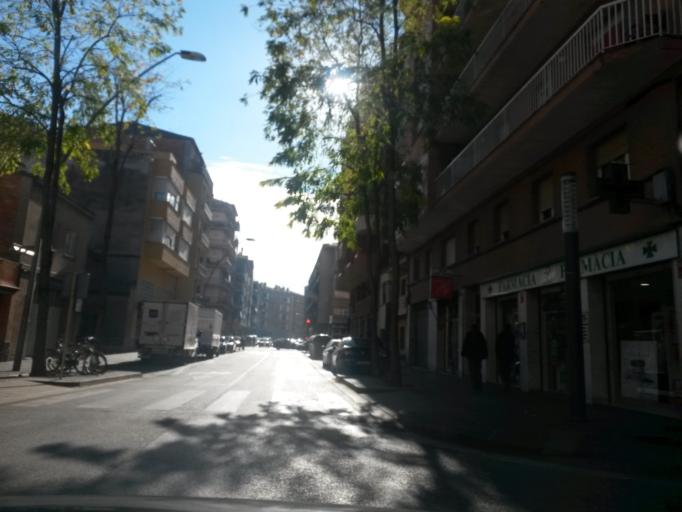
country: ES
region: Catalonia
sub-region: Provincia de Girona
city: Salt
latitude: 41.9752
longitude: 2.8028
